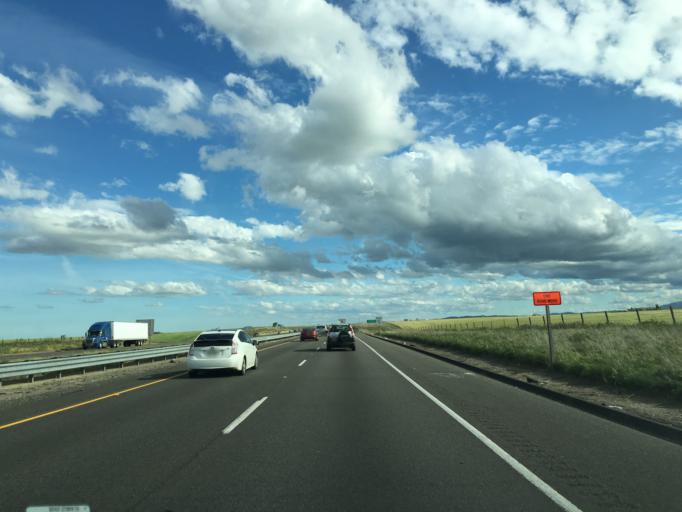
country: US
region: California
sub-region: Merced County
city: Los Banos
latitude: 37.0521
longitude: -120.9657
